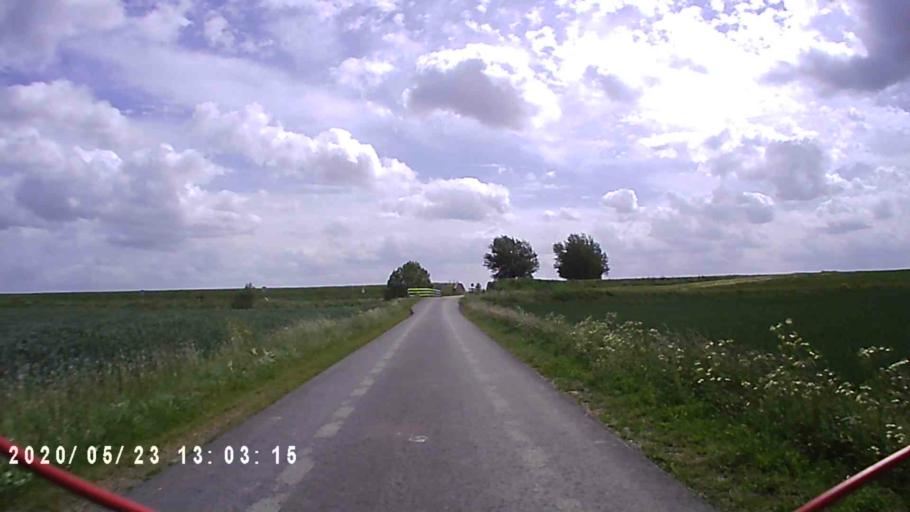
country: NL
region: Groningen
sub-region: Gemeente  Oldambt
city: Winschoten
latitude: 53.2878
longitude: 7.0692
